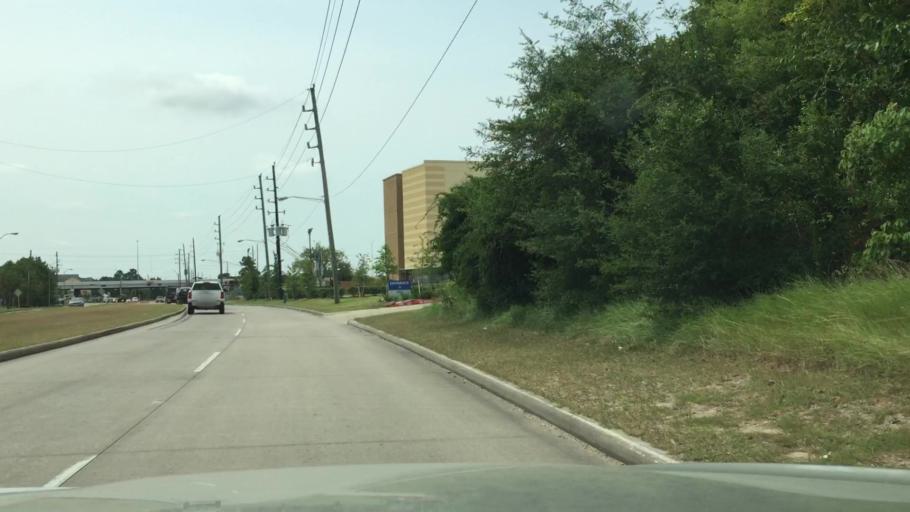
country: US
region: Texas
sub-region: Harris County
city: Jersey Village
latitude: 29.9329
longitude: -95.5459
